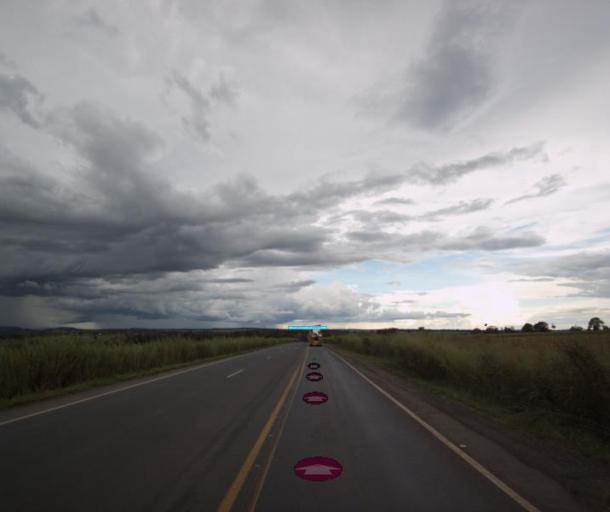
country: BR
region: Goias
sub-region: Itapaci
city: Itapaci
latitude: -15.0110
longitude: -49.4183
